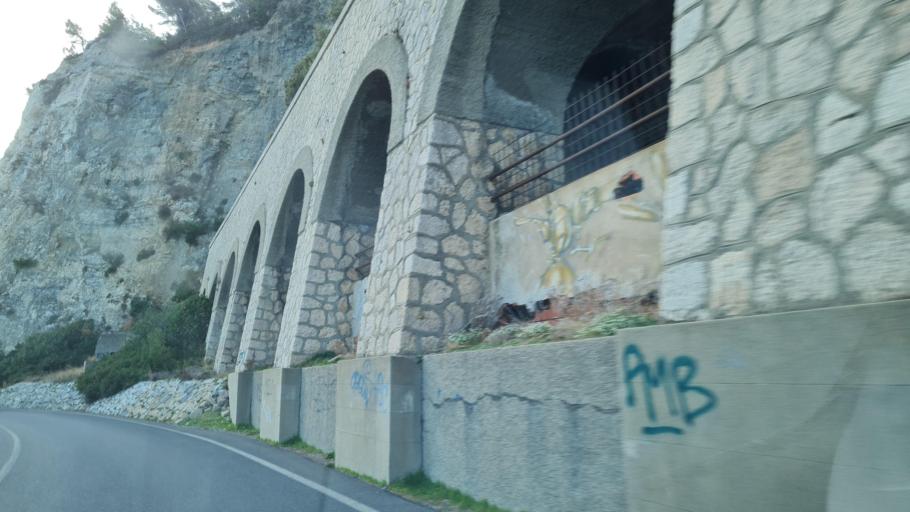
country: IT
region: Liguria
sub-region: Provincia di Savona
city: Noli
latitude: 44.1876
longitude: 8.4094
